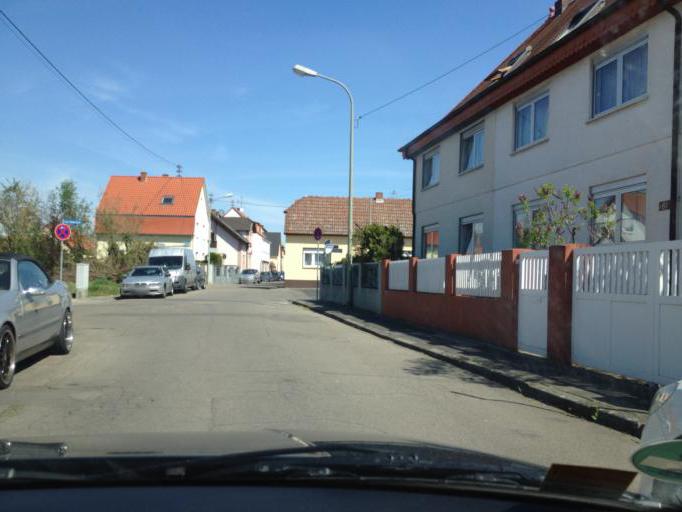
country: DE
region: Rheinland-Pfalz
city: Neuhofen
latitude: 49.4180
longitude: 8.4248
